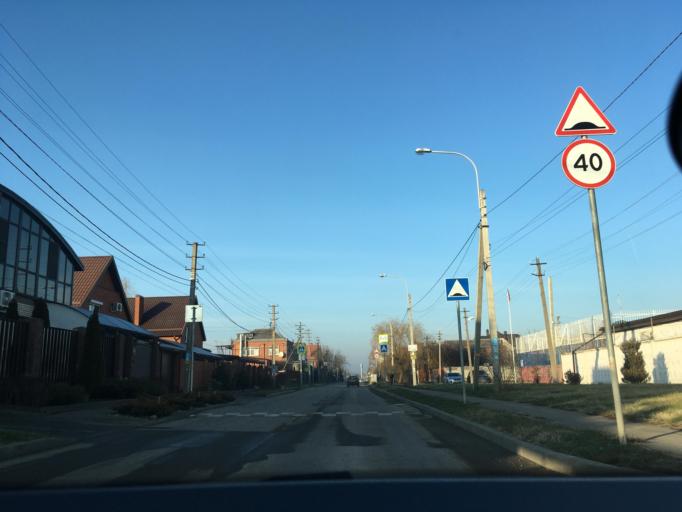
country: RU
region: Krasnodarskiy
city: Krasnodar
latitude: 45.1189
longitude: 39.0144
